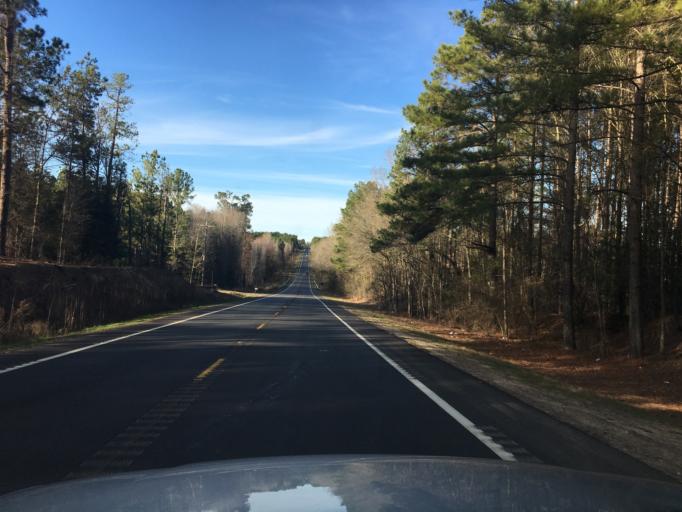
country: US
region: South Carolina
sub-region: Aiken County
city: Aiken
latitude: 33.7015
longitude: -81.6583
